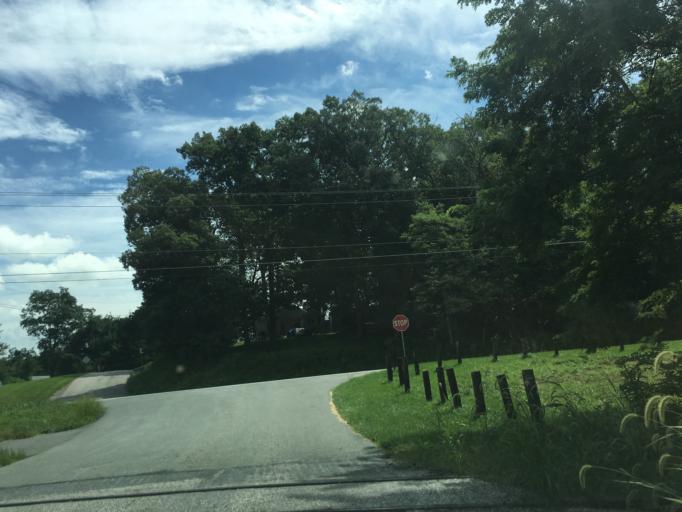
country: US
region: Pennsylvania
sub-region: York County
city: New Freedom
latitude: 39.7497
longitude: -76.6882
